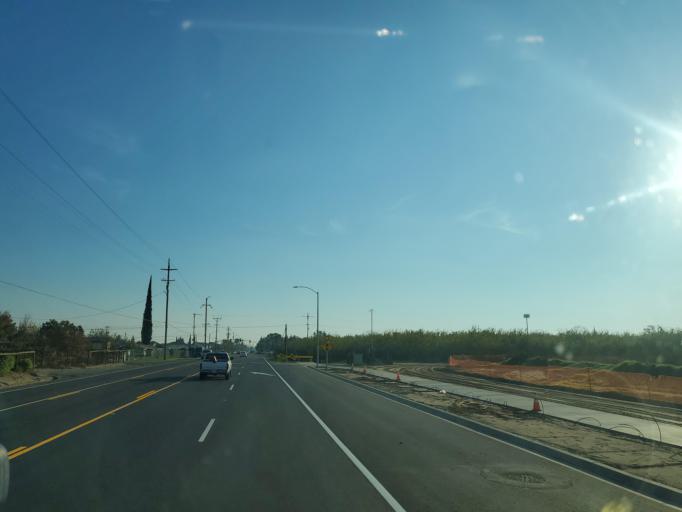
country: US
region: California
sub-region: San Joaquin County
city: Lathrop
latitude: 37.8289
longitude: -121.2540
